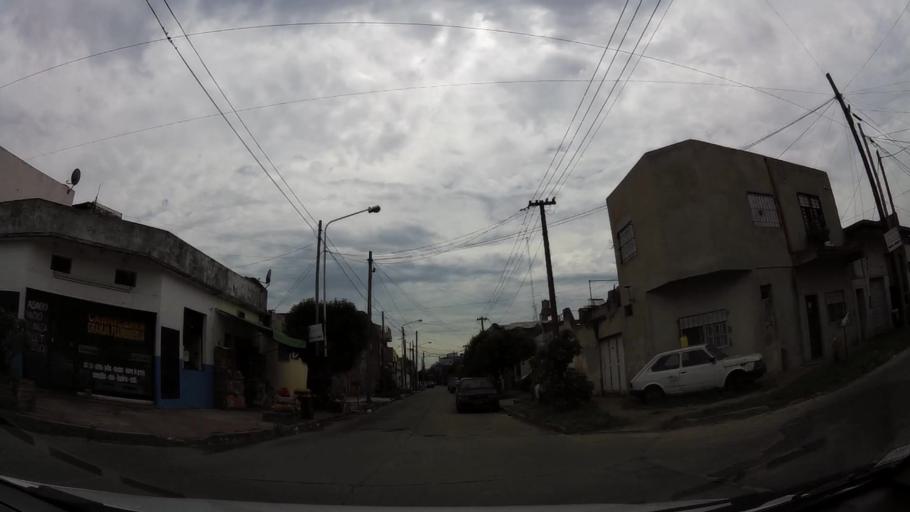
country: AR
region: Buenos Aires F.D.
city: Villa Lugano
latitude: -34.6831
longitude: -58.5086
